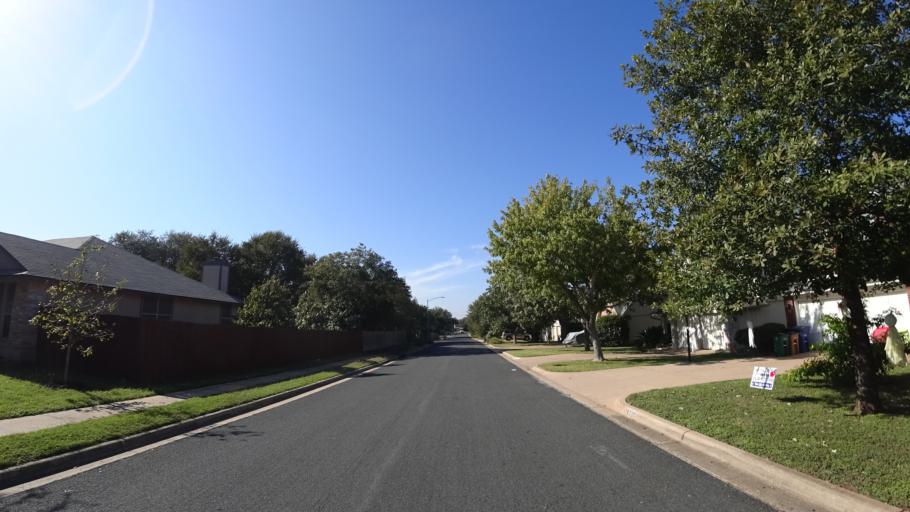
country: US
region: Texas
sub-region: Travis County
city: Shady Hollow
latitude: 30.2005
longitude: -97.8507
